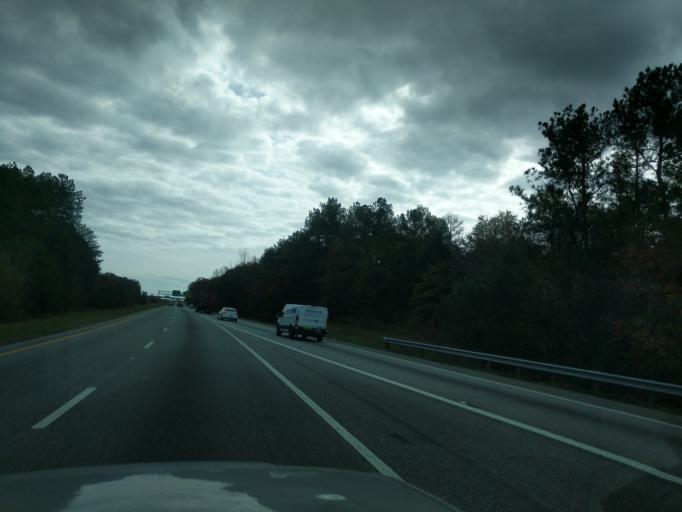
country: US
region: South Carolina
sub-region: Laurens County
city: Clinton
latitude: 34.5131
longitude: -81.8701
